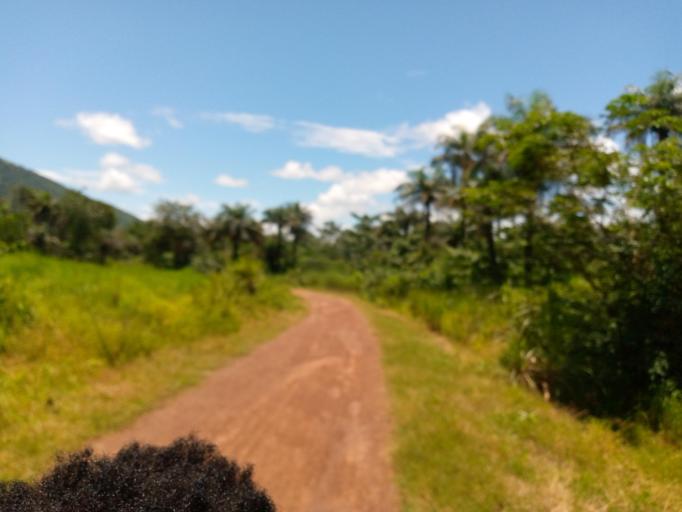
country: SL
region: Northern Province
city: Binkolo
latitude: 9.0985
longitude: -12.1433
